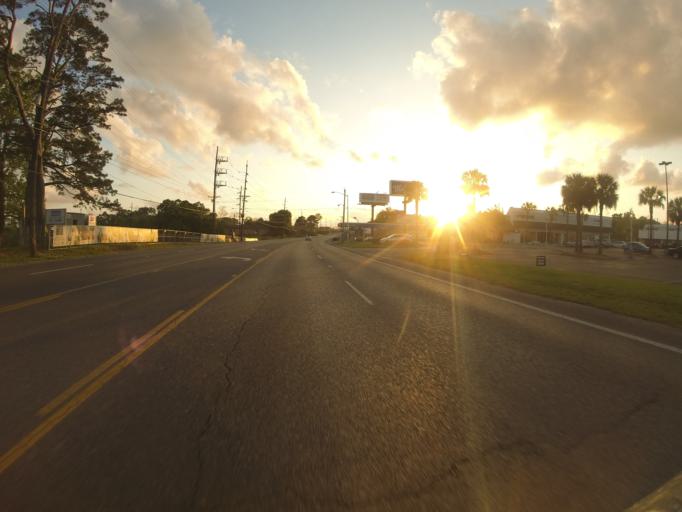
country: US
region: Louisiana
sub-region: Lafayette Parish
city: Lafayette
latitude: 30.2055
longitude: -92.0415
